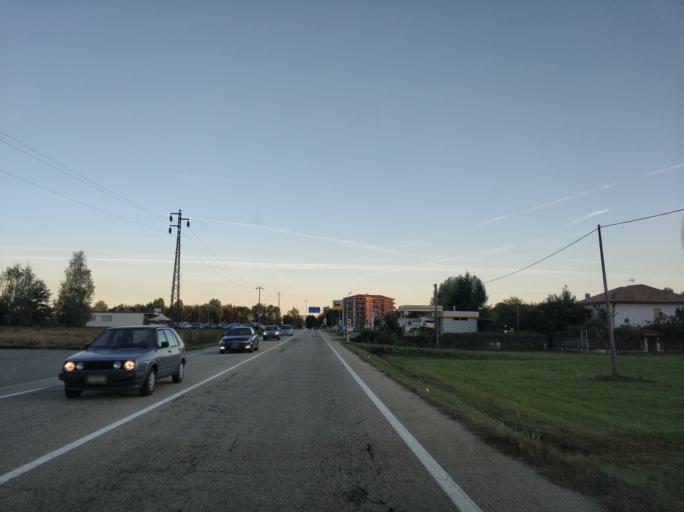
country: IT
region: Piedmont
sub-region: Provincia di Torino
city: Fiano
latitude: 45.2111
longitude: 7.5466
